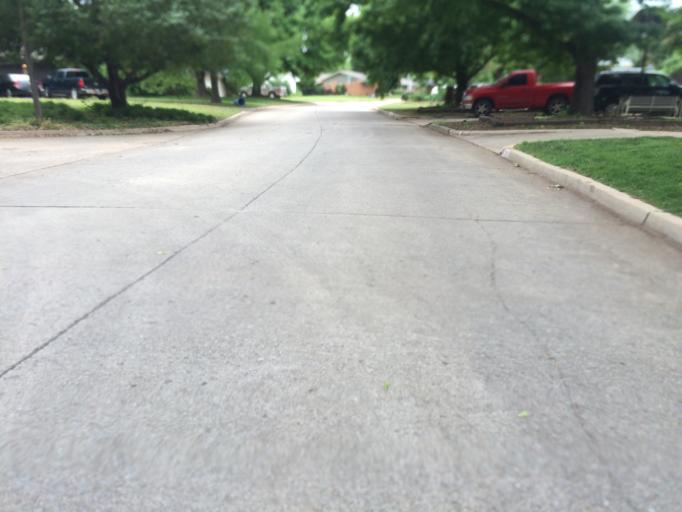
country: US
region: Oklahoma
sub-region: Cleveland County
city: Norman
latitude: 35.2115
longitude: -97.4785
